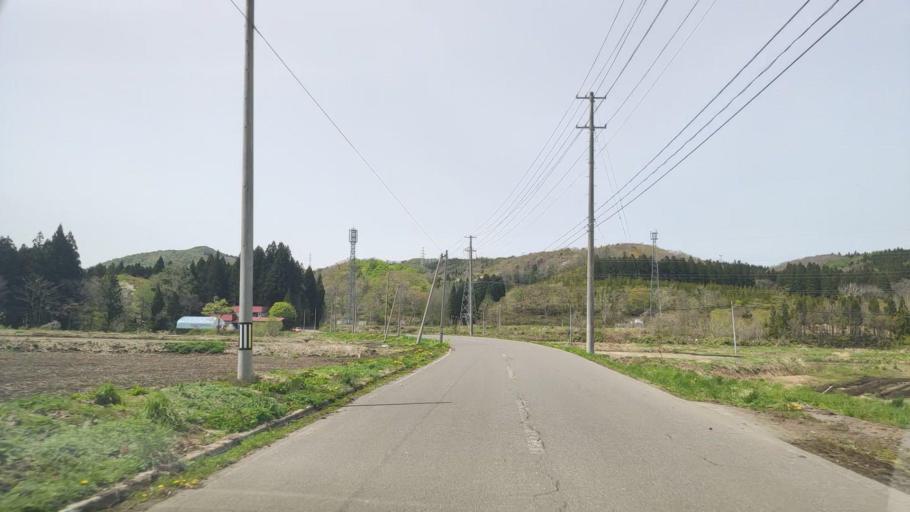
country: JP
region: Aomori
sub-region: Misawa Shi
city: Inuotose
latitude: 40.7893
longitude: 141.1028
